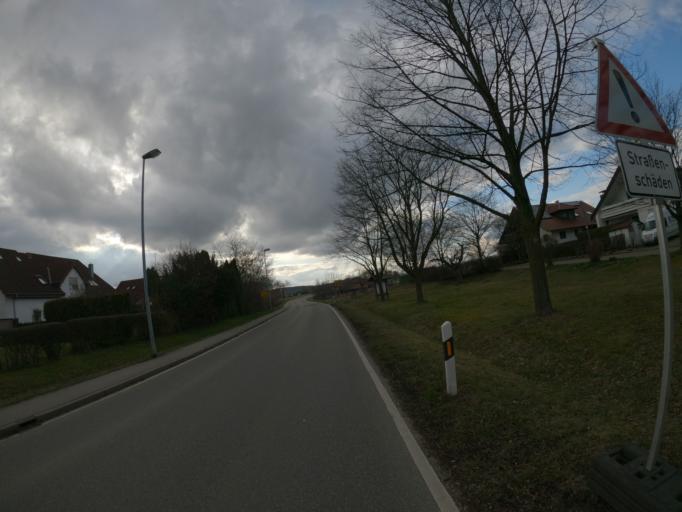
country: DE
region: Baden-Wuerttemberg
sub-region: Regierungsbezirk Stuttgart
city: Heiningen
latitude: 48.6606
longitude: 9.6392
